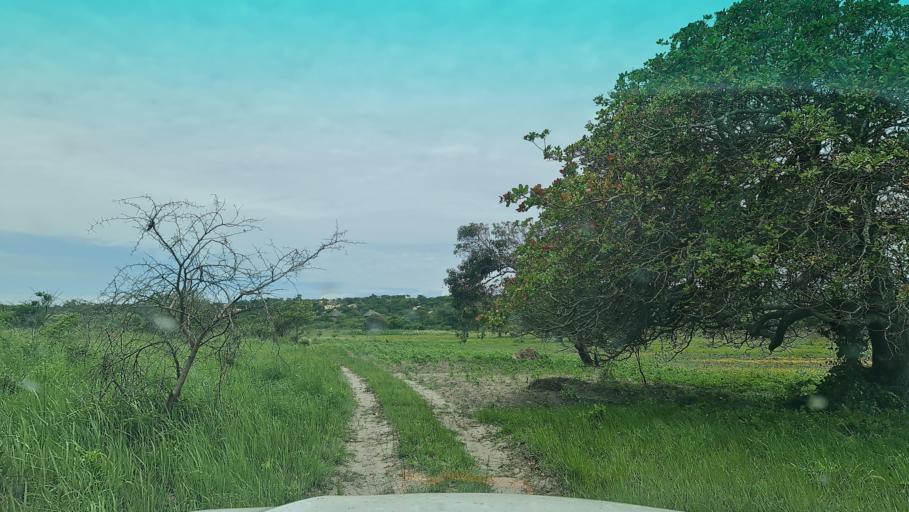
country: MZ
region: Maputo
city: Manhica
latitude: -25.6380
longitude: 32.7718
